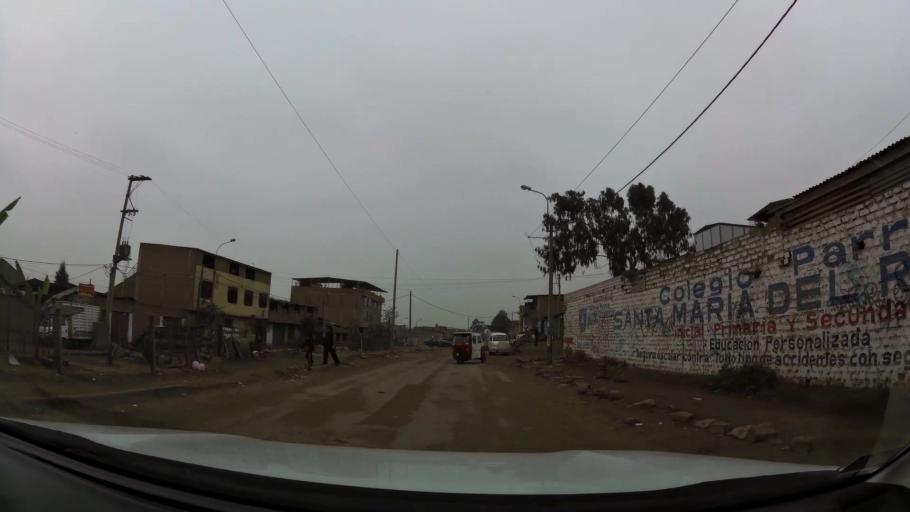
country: PE
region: Lima
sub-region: Lima
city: Surco
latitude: -12.1977
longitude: -76.9305
